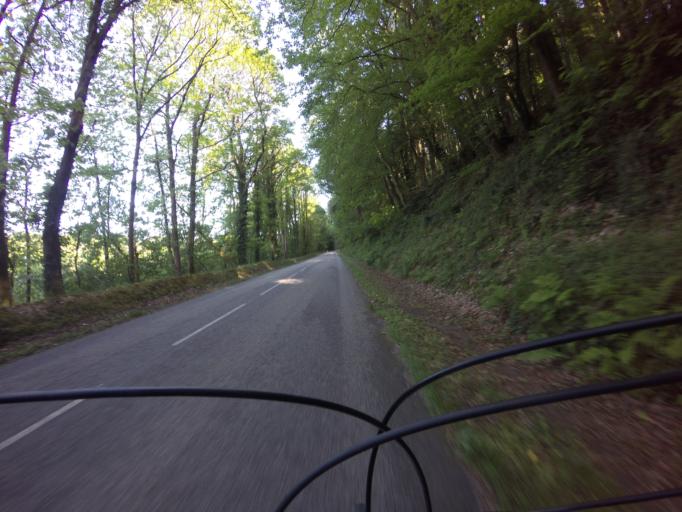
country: FR
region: Brittany
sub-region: Departement du Finistere
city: Quimper
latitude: 48.0234
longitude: -4.1412
